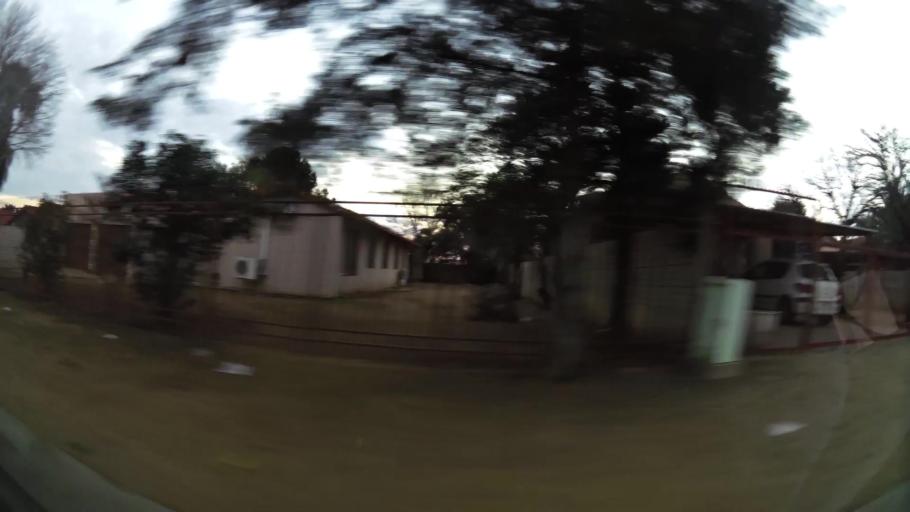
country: ZA
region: Orange Free State
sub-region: Mangaung Metropolitan Municipality
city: Bloemfontein
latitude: -29.1706
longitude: 26.1932
